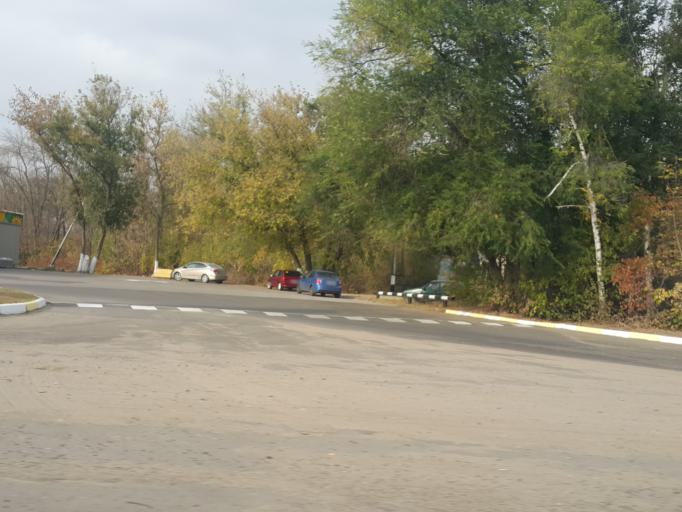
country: RU
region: Tambov
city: Bokino
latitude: 52.6640
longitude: 41.4496
